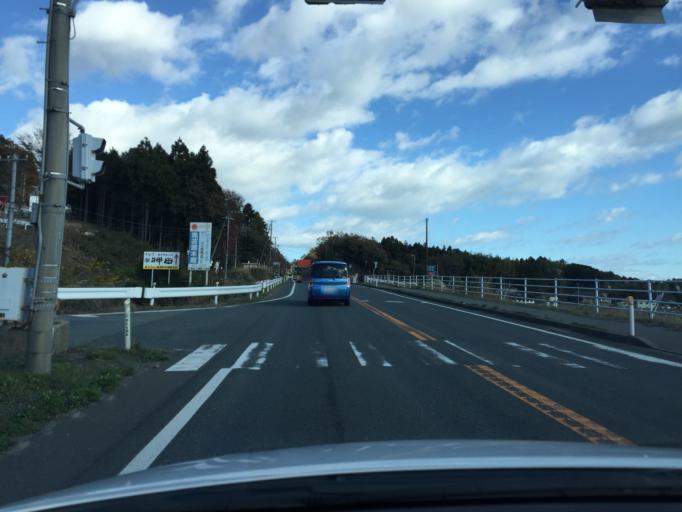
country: JP
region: Fukushima
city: Namie
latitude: 37.3252
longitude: 141.0148
